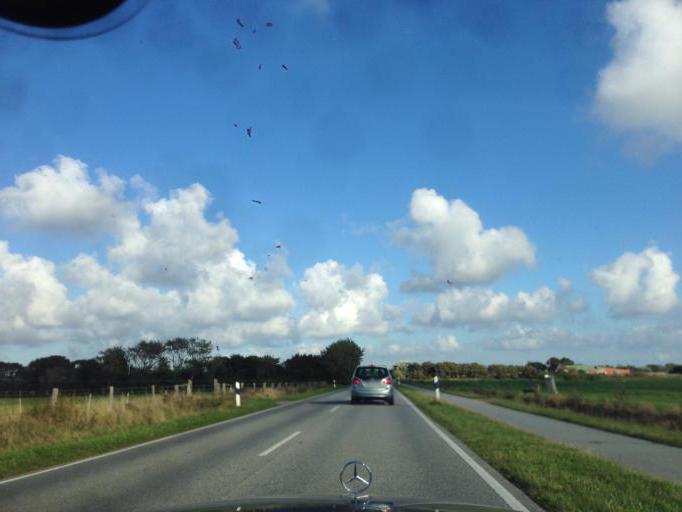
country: DE
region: Schleswig-Holstein
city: Sylt-Ost
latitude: 54.8716
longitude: 8.4056
